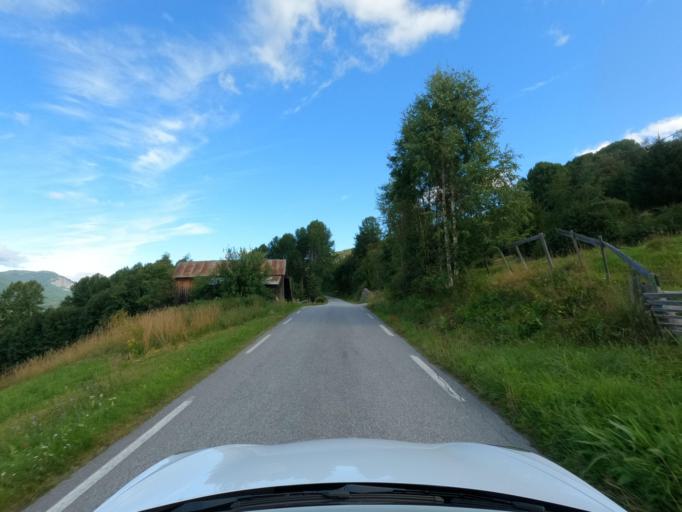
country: NO
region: Buskerud
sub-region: Nore og Uvdal
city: Rodberg
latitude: 60.0369
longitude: 8.8325
